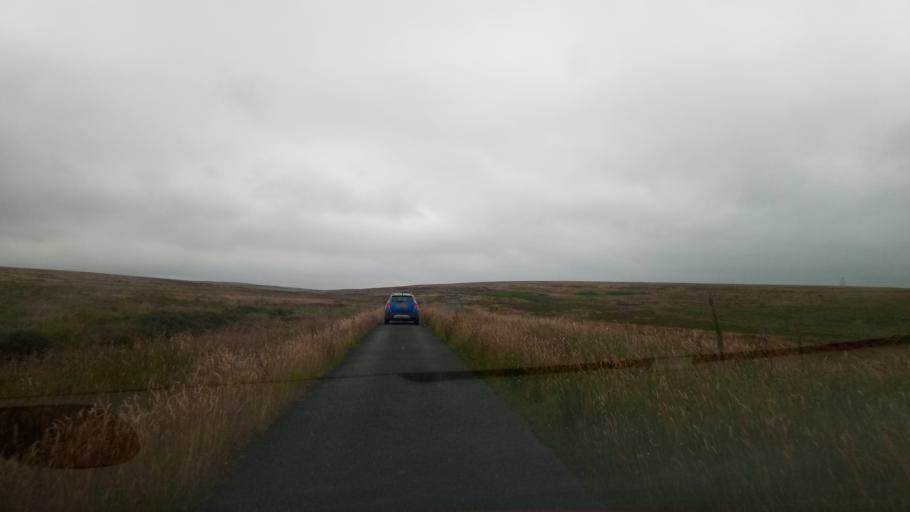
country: GB
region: Scotland
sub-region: Dumfries and Galloway
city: Langholm
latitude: 55.1692
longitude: -2.9235
